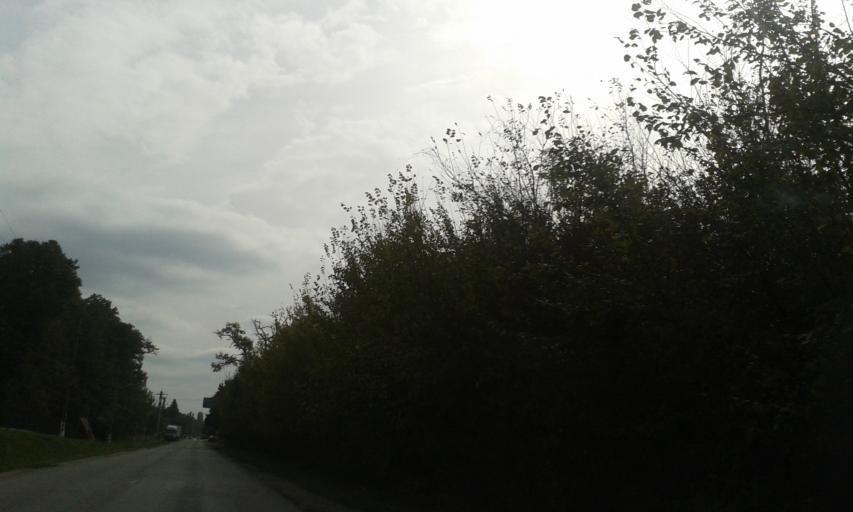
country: RO
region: Gorj
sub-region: Comuna Targu Carbunesti
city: Targu Carbunesti
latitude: 44.9664
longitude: 23.5047
